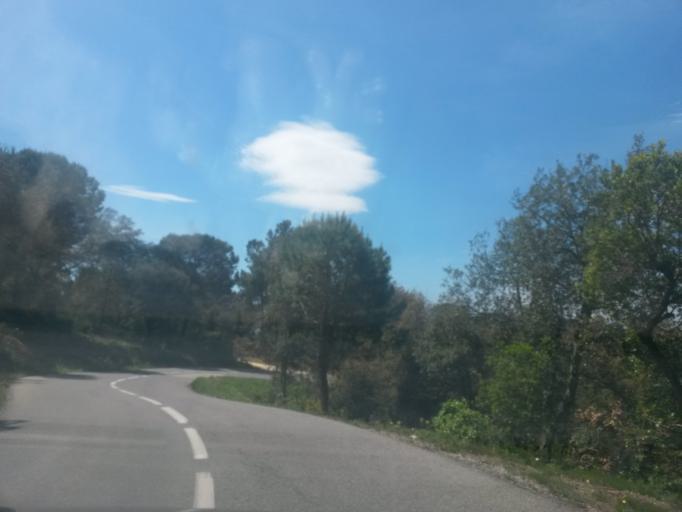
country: ES
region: Catalonia
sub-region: Provincia de Girona
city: Cassa de la Selva
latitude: 41.9050
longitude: 2.9092
